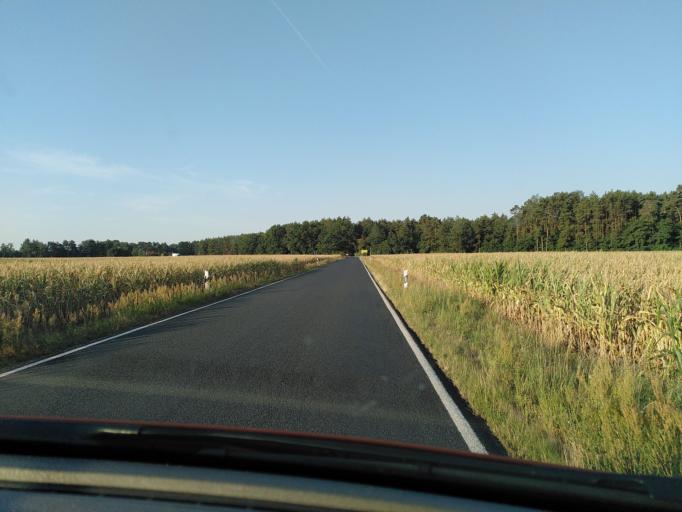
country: DE
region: Saxony
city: Konigswartha
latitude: 51.3054
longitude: 14.3168
